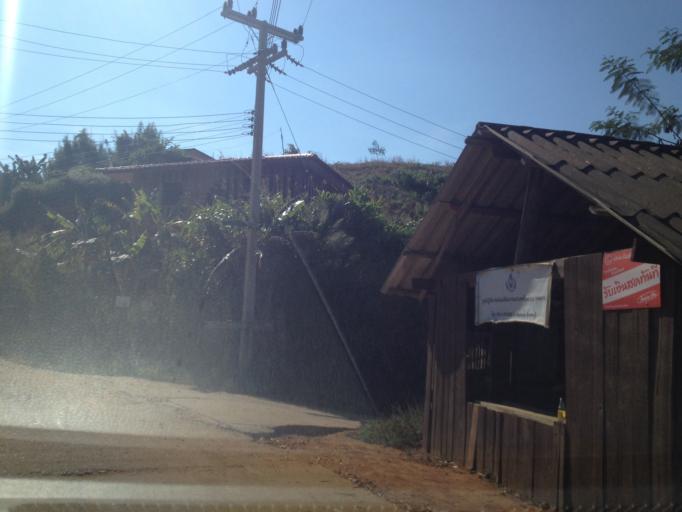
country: TH
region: Mae Hong Son
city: Ban Huai I Huak
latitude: 18.0413
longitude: 98.1654
